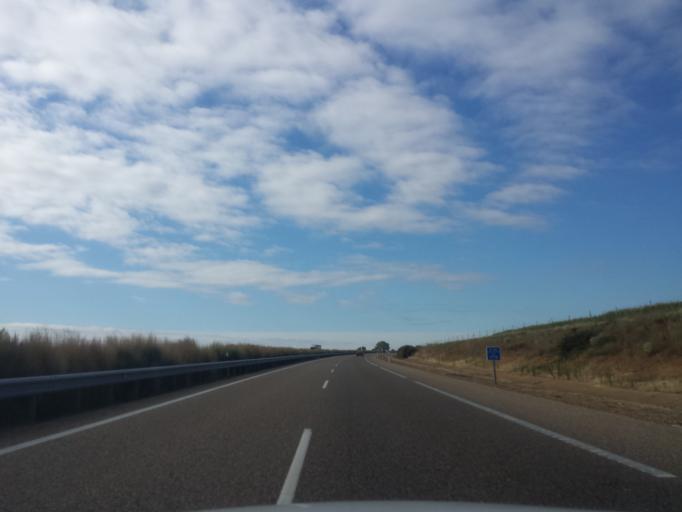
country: ES
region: Castille and Leon
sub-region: Provincia de Leon
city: Villademor de la Vega
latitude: 42.2760
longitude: -5.5898
